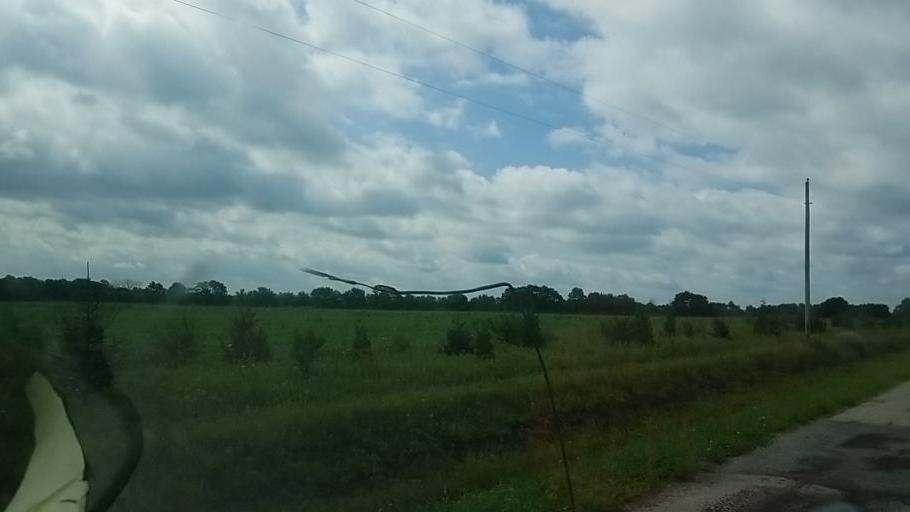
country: US
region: Ohio
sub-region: Madison County
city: Mount Sterling
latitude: 39.7770
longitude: -83.2610
